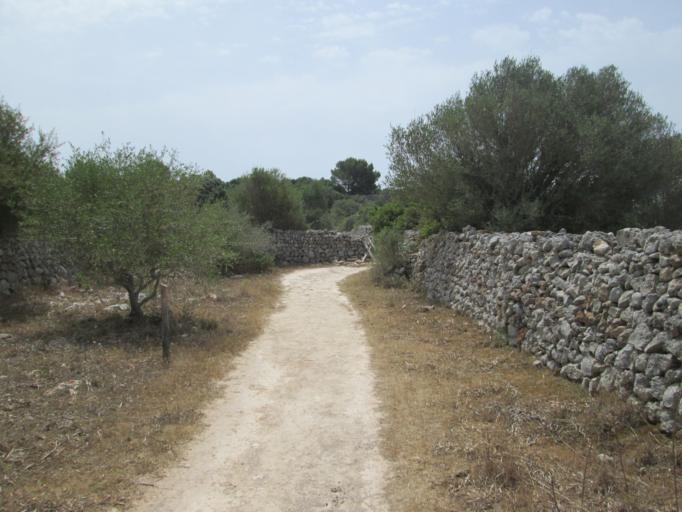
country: ES
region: Balearic Islands
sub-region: Illes Balears
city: Es Migjorn Gran
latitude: 39.9354
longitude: 4.0381
